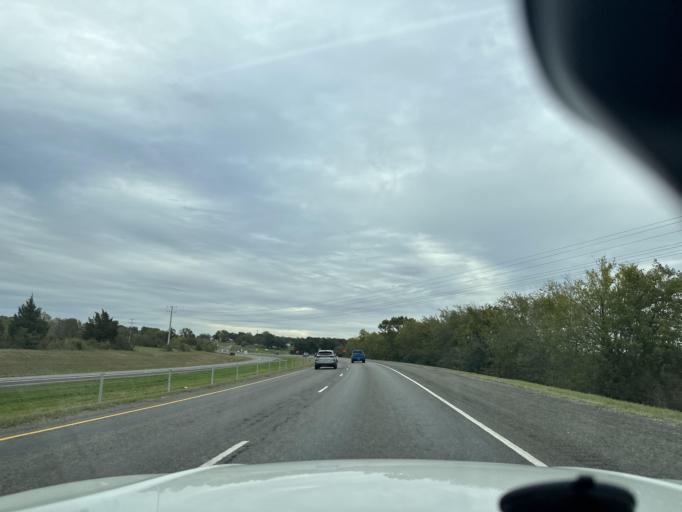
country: US
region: Texas
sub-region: Burleson County
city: Somerville
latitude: 30.1755
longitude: -96.5981
